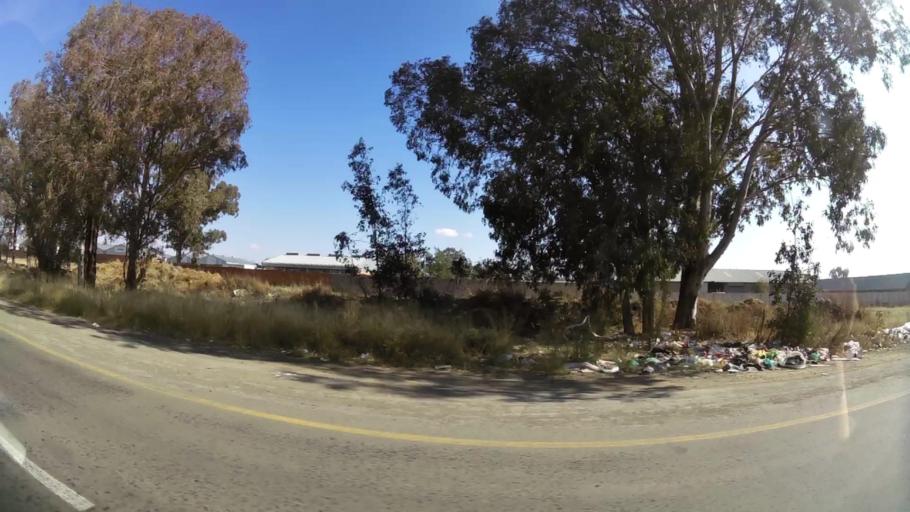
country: ZA
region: Orange Free State
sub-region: Mangaung Metropolitan Municipality
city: Bloemfontein
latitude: -29.1304
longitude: 26.2671
